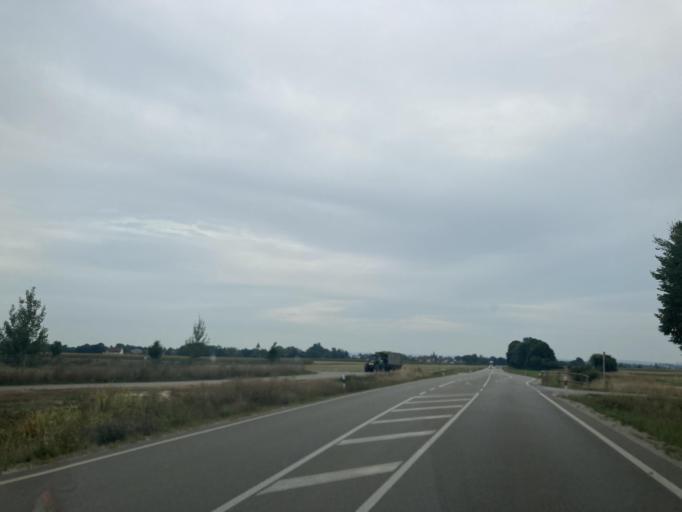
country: DE
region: Bavaria
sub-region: Swabia
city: Noerdlingen
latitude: 48.8676
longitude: 10.5242
